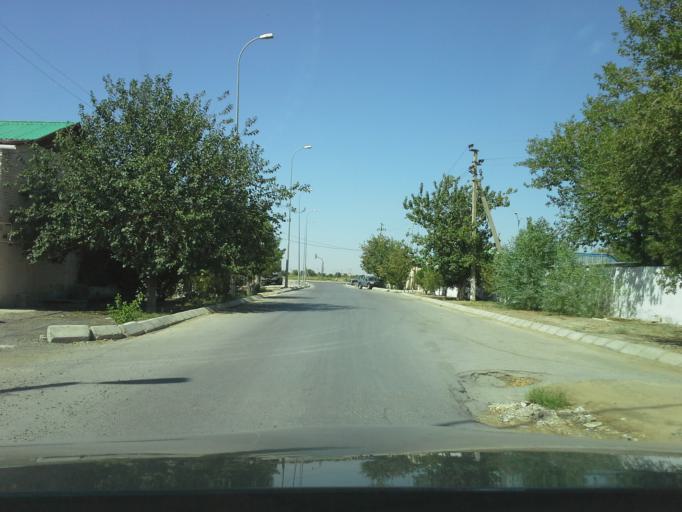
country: TM
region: Ahal
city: Ashgabat
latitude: 38.0090
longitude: 58.3040
